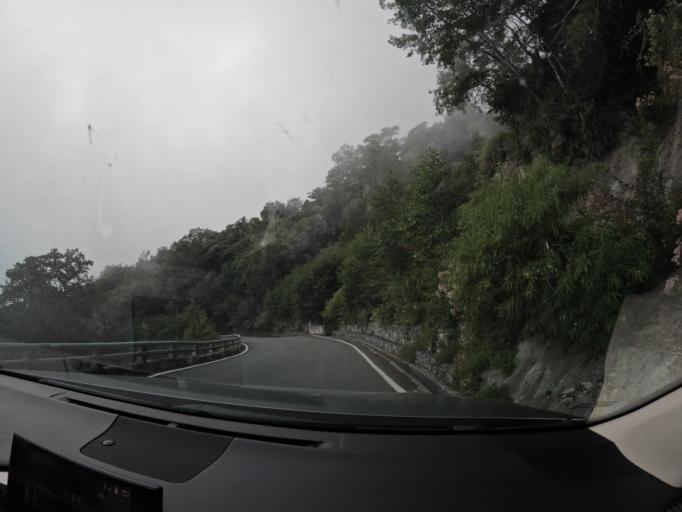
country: TW
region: Taiwan
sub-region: Taitung
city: Taitung
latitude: 23.2442
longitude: 120.9870
